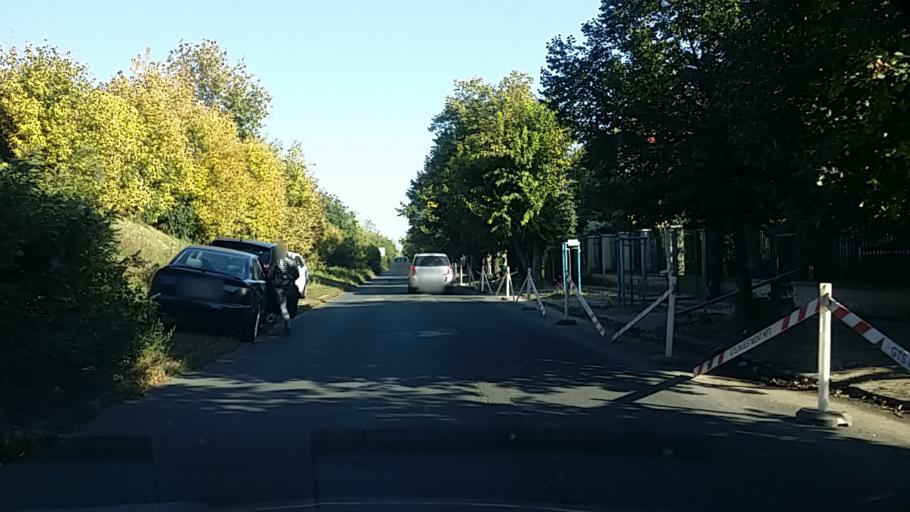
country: HU
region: Budapest
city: Budapest XI. keruelet
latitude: 47.4725
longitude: 19.0364
